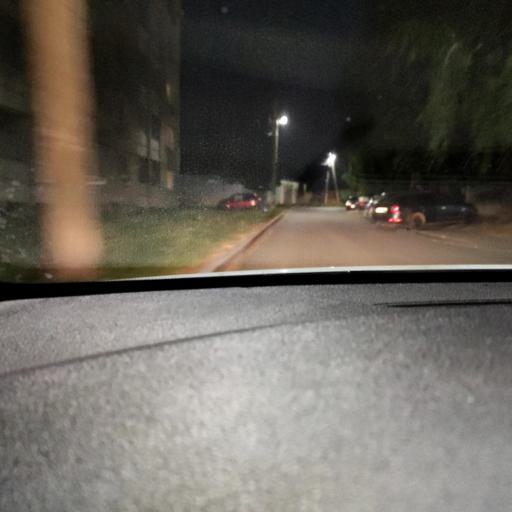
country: RU
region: Tatarstan
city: Vysokaya Gora
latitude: 55.8632
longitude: 49.2326
